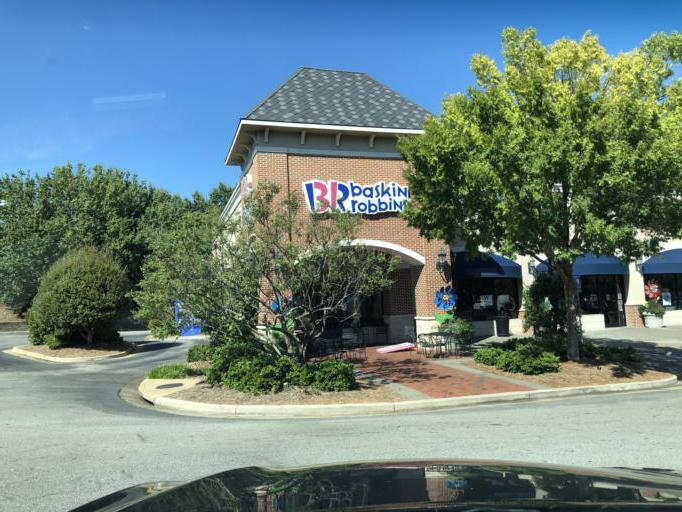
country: US
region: Alabama
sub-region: Russell County
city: Phenix City
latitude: 32.5218
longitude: -84.9585
